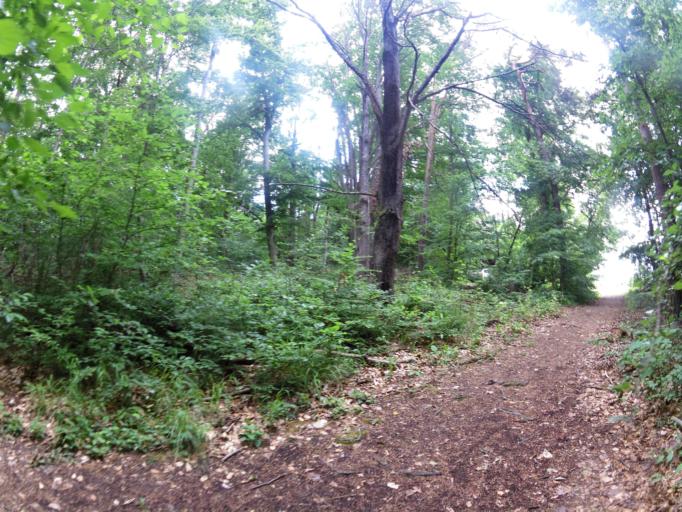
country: DE
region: Bavaria
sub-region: Regierungsbezirk Unterfranken
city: Thungersheim
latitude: 49.8757
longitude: 9.8696
